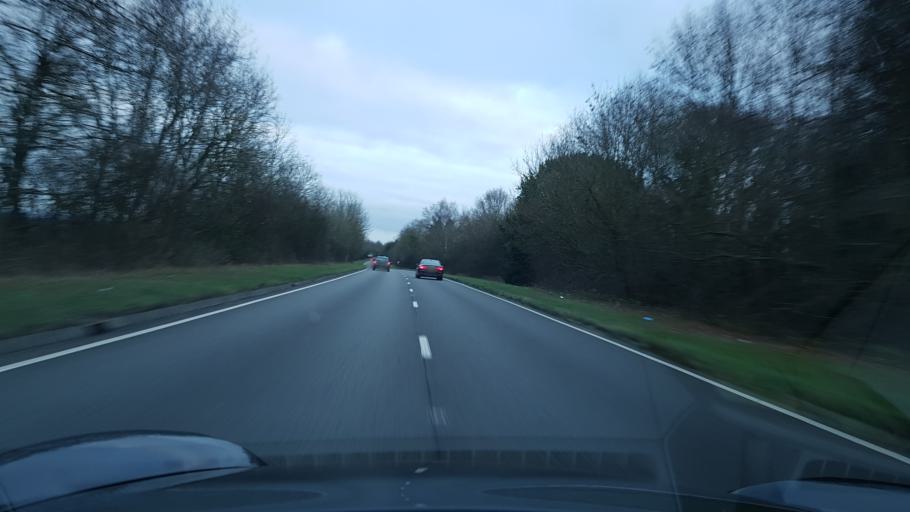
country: GB
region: England
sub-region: Surrey
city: Normandy
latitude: 51.2264
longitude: -0.6735
